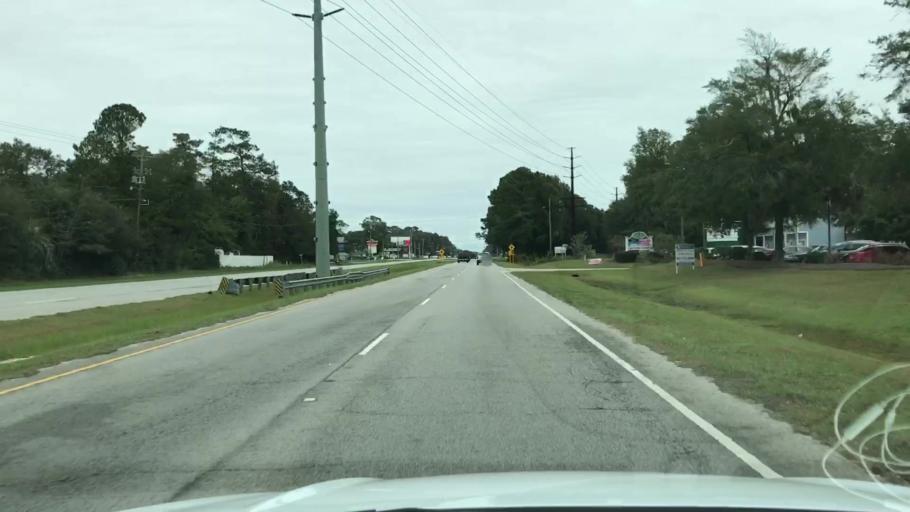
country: US
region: South Carolina
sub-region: Georgetown County
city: Murrells Inlet
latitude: 33.5325
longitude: -79.0599
